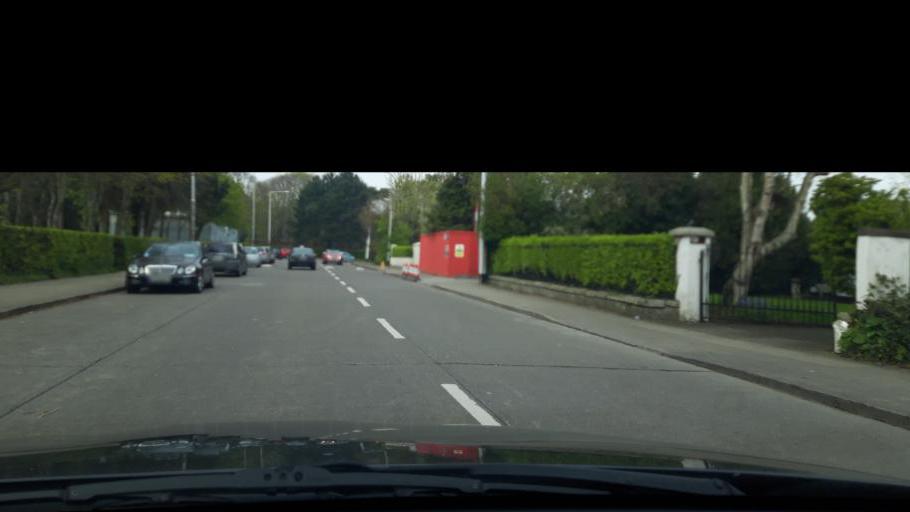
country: IE
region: Leinster
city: Dollymount
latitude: 53.3689
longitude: -6.1820
